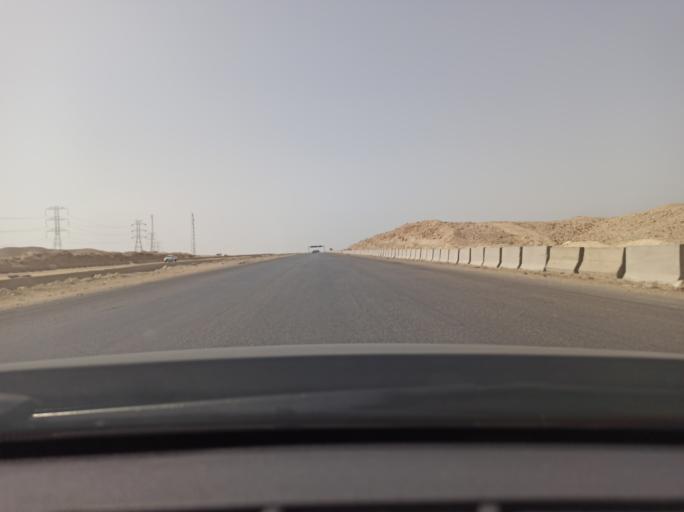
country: EG
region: Al Jizah
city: As Saff
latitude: 29.5443
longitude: 31.3923
